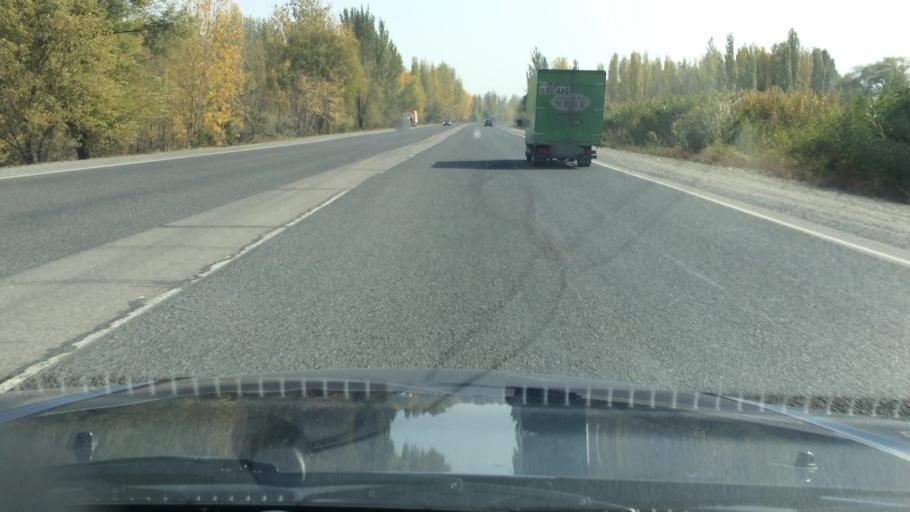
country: KG
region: Chuy
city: Ivanovka
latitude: 42.9389
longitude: 74.9807
